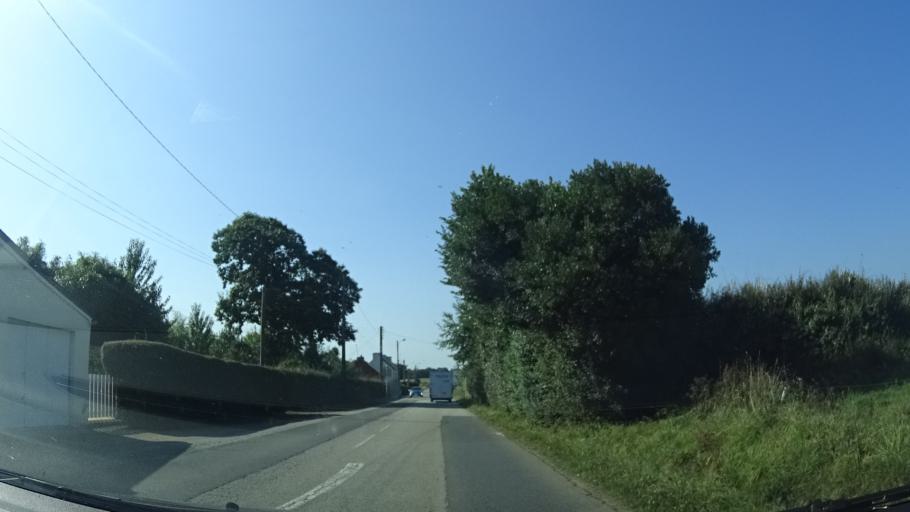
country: FR
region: Brittany
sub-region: Departement du Finistere
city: Cast
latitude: 48.1521
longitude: -4.1425
